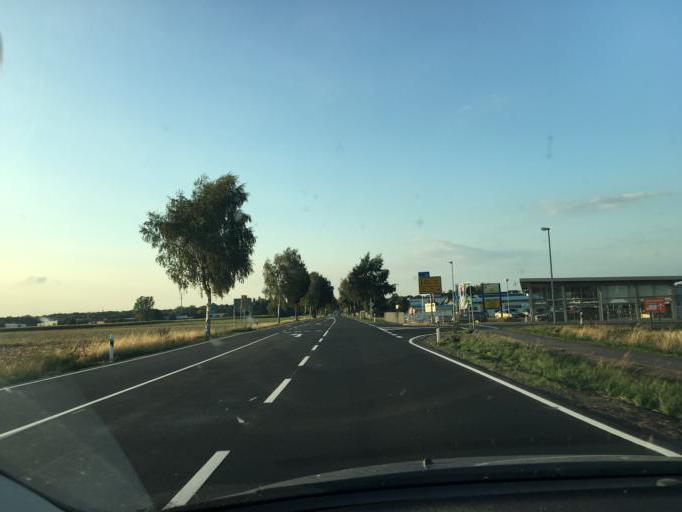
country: DE
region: Lower Saxony
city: Bergen
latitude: 52.7927
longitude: 9.9714
